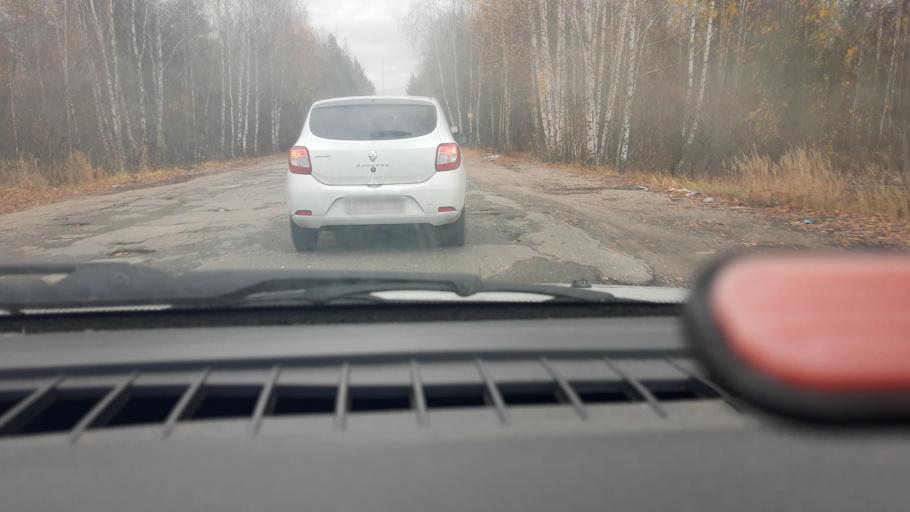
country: RU
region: Nizjnij Novgorod
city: Babino
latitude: 56.3051
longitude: 43.6611
